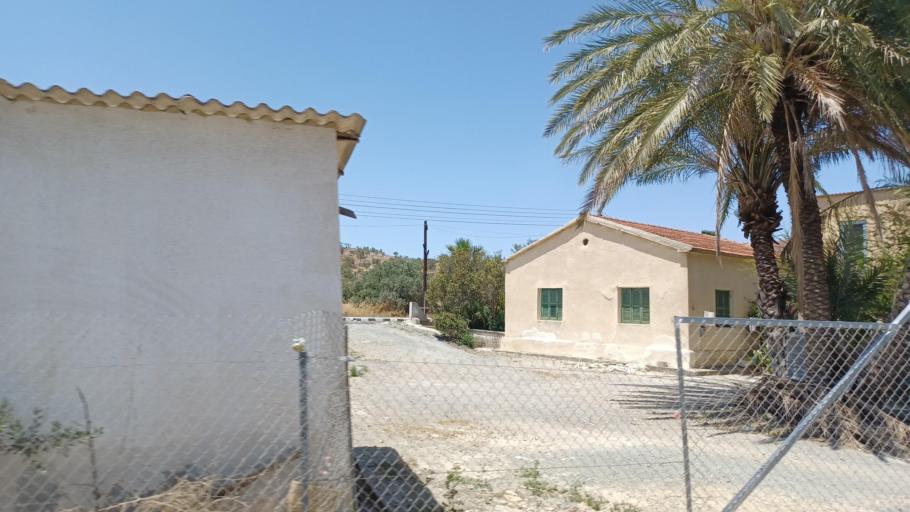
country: CY
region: Larnaka
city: Pyla
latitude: 35.0092
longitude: 33.6915
